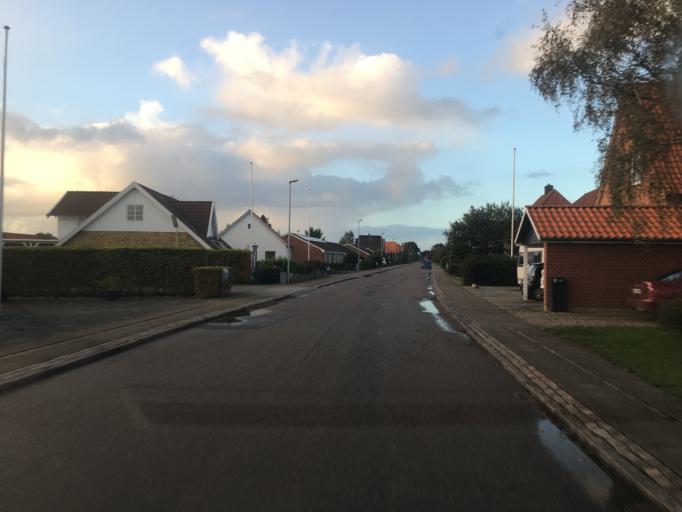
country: DK
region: South Denmark
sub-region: Tonder Kommune
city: Tonder
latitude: 54.9315
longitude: 8.8544
